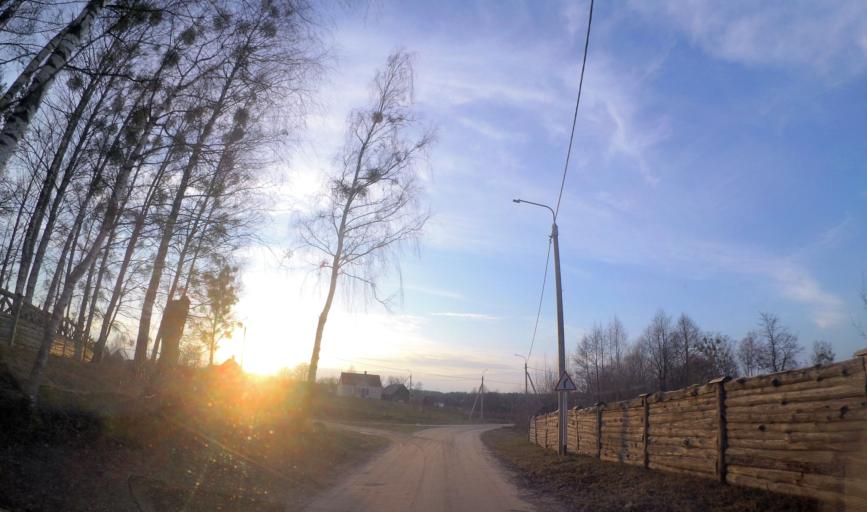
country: LT
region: Alytaus apskritis
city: Druskininkai
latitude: 53.9109
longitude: 24.1807
